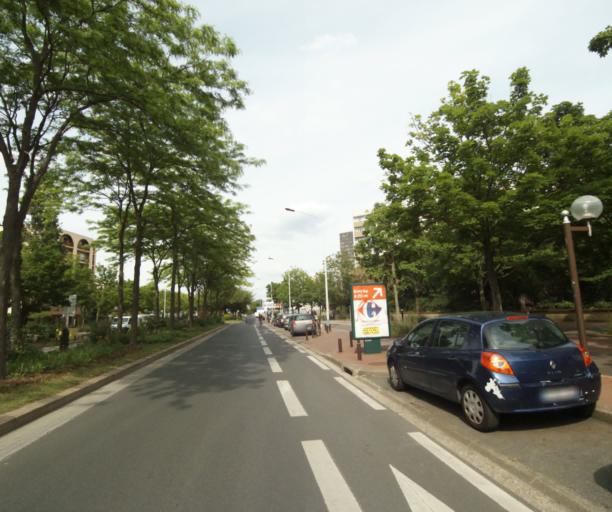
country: FR
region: Ile-de-France
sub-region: Departement des Hauts-de-Seine
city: Asnieres-sur-Seine
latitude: 48.9242
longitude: 2.2888
